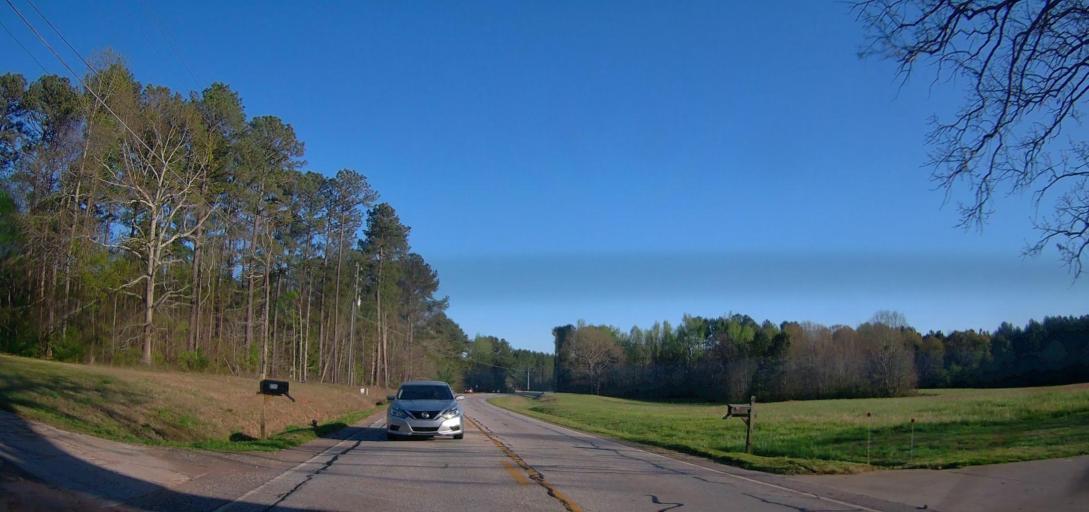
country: US
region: Georgia
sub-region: Newton County
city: Oakwood
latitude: 33.4583
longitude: -83.9046
